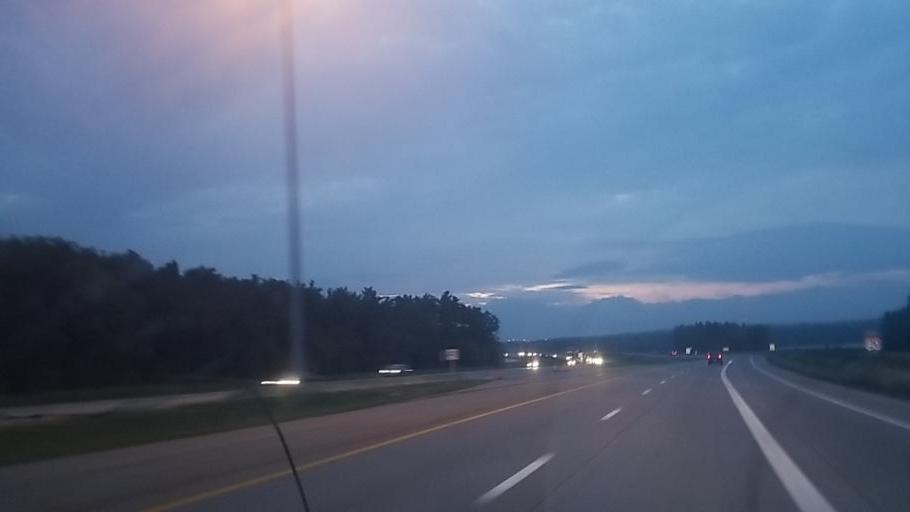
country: US
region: Ohio
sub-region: Mahoning County
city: Austintown
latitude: 41.1111
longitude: -80.8220
